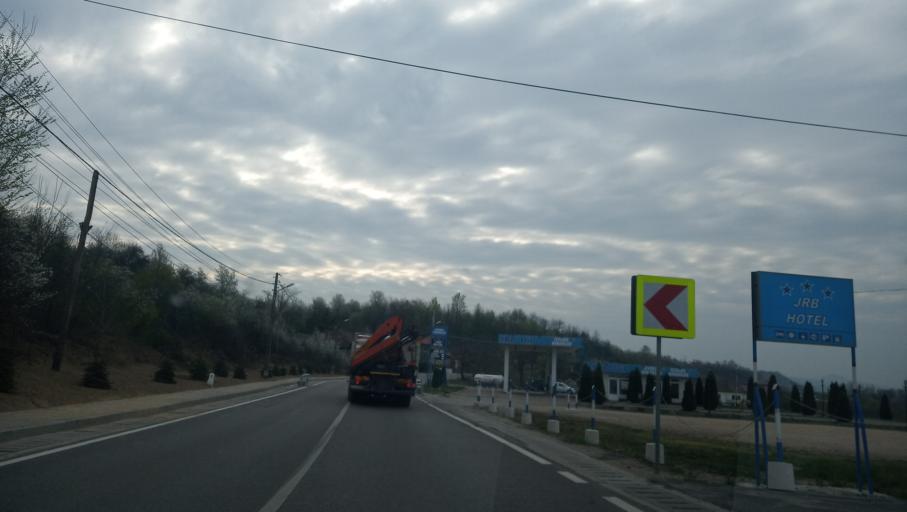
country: RO
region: Bihor
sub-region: Comuna Lunca
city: Lunca
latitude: 46.5283
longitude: 22.4592
